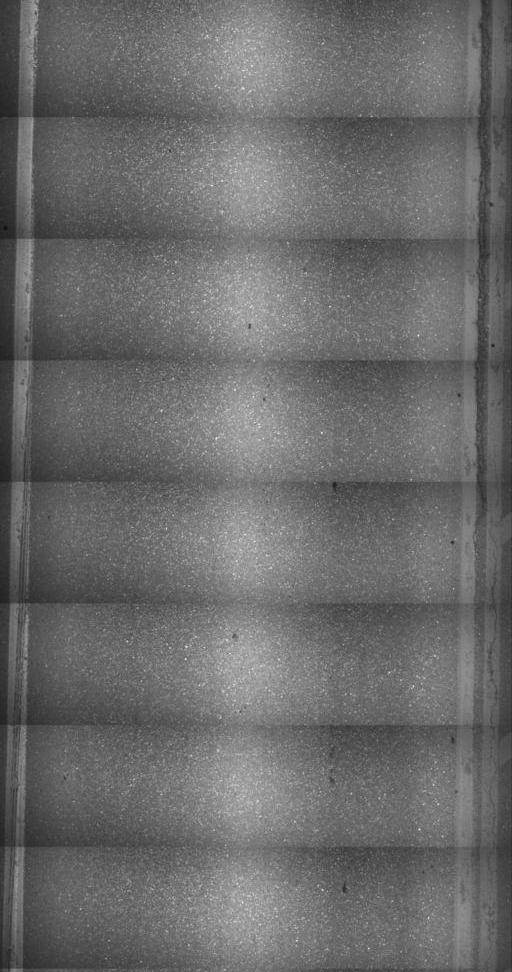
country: US
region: Vermont
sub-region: Chittenden County
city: Williston
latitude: 44.4447
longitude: -73.1009
